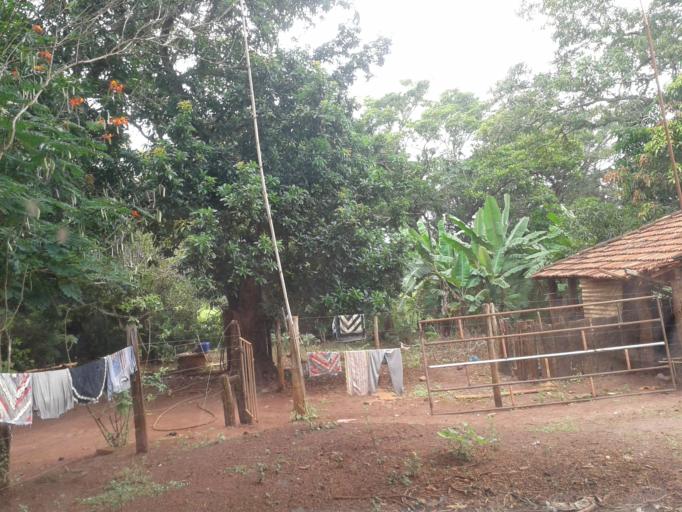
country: BR
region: Minas Gerais
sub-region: Capinopolis
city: Capinopolis
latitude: -18.7956
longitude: -49.7860
